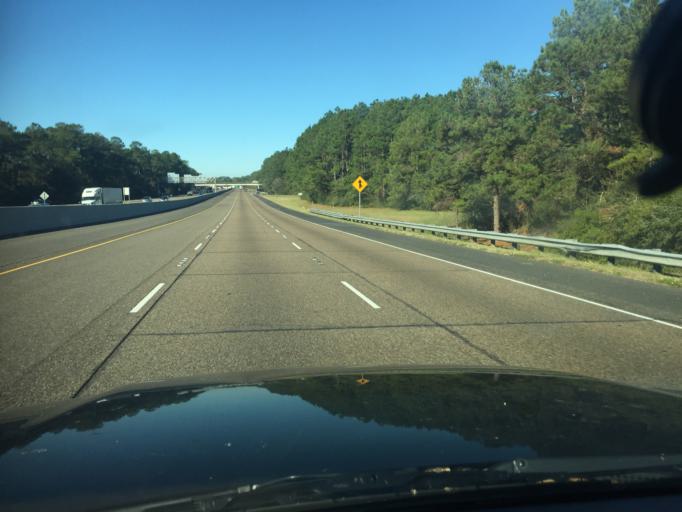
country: US
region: Louisiana
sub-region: Saint Tammany Parish
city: Slidell
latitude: 30.3071
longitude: -89.7436
